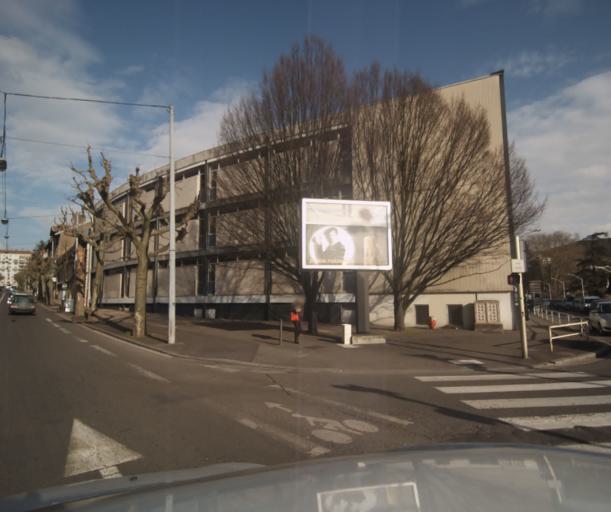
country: FR
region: Franche-Comte
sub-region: Departement du Doubs
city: Besancon
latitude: 47.2429
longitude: 6.0259
